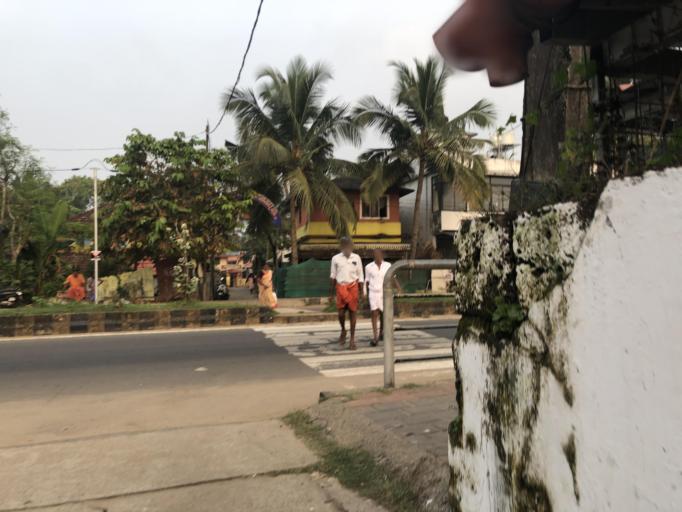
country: IN
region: Kerala
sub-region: Kozhikode
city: Kozhikode
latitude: 11.2673
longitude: 75.7666
